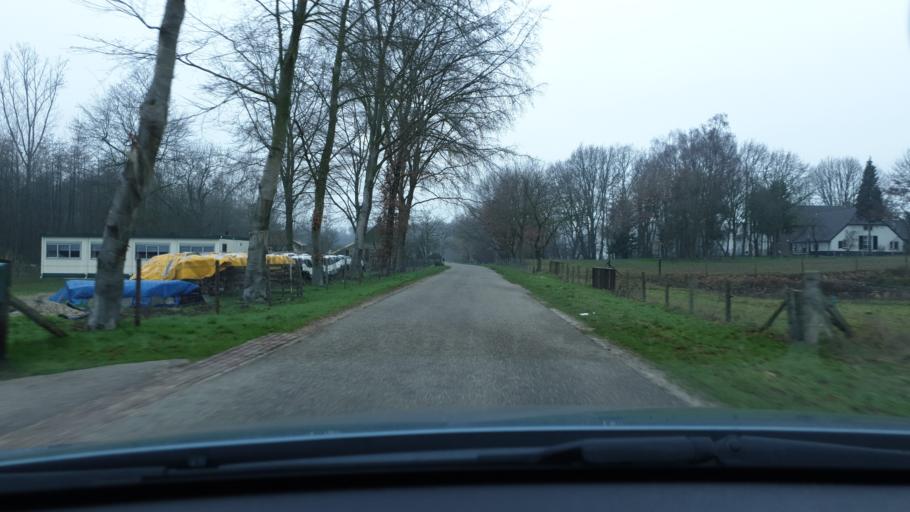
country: NL
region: Gelderland
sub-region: Gemeente Wijchen
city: Bergharen
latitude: 51.8627
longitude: 5.6630
